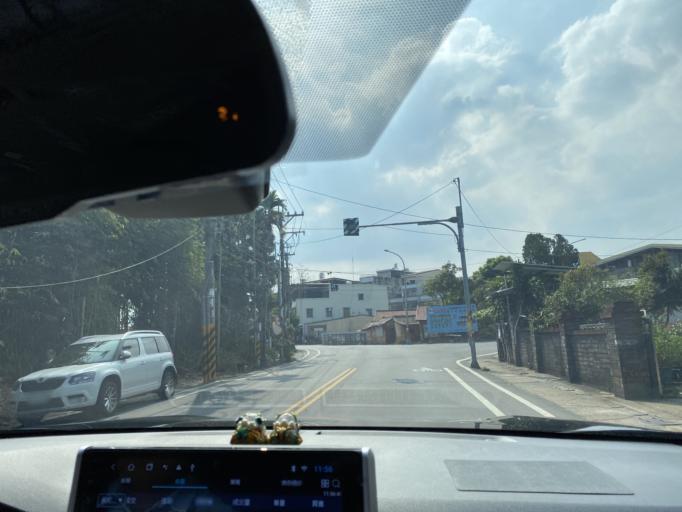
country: TW
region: Taiwan
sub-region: Nantou
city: Nantou
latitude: 23.8414
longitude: 120.6950
